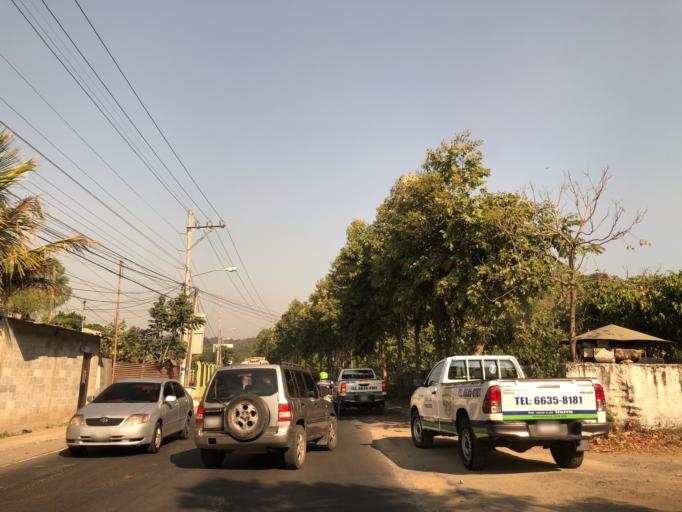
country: GT
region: Guatemala
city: Villa Canales
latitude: 14.4886
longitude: -90.5350
